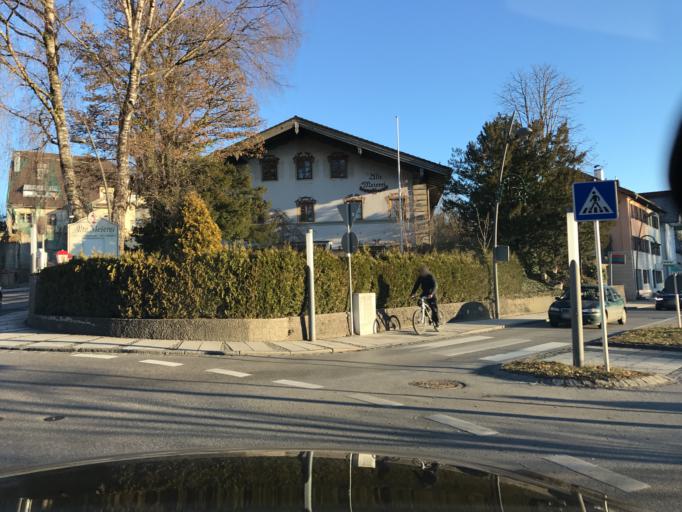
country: DE
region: Bavaria
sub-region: Upper Bavaria
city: Bad Aibling
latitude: 47.8624
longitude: 12.0119
